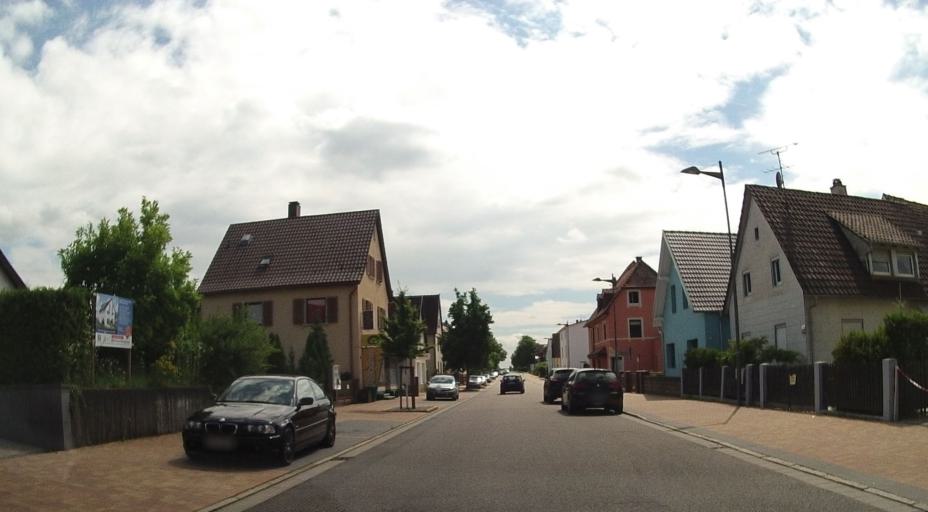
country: DE
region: Baden-Wuerttemberg
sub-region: Karlsruhe Region
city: Durmersheim
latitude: 48.9266
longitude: 8.2655
